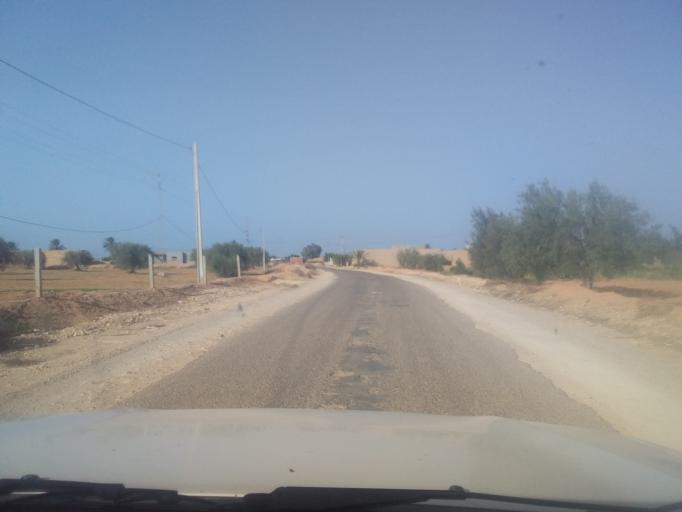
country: TN
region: Qabis
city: Matmata
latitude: 33.5888
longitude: 10.2777
